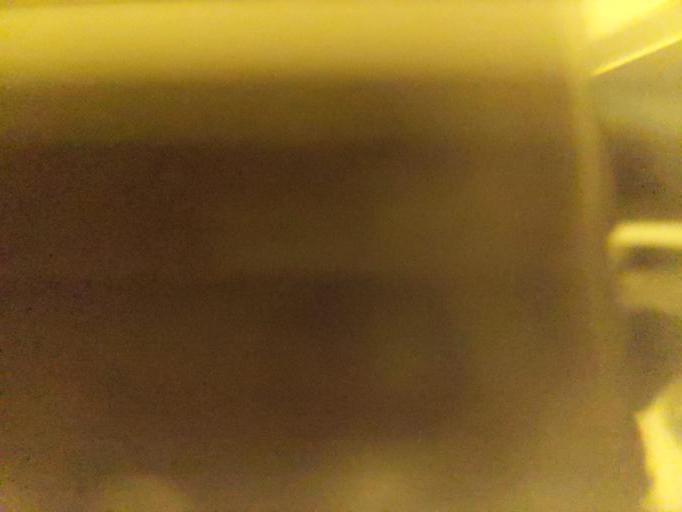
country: JP
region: Shizuoka
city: Atami
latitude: 35.1018
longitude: 139.0399
